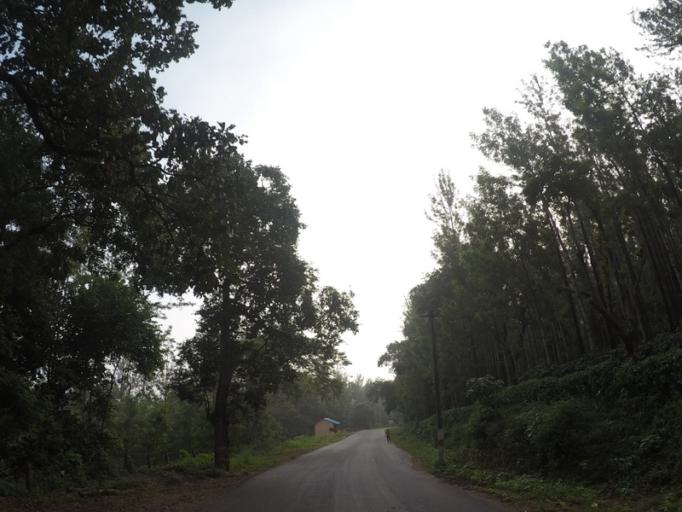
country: IN
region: Karnataka
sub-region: Chikmagalur
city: Chikmagalur
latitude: 13.3820
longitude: 75.7545
